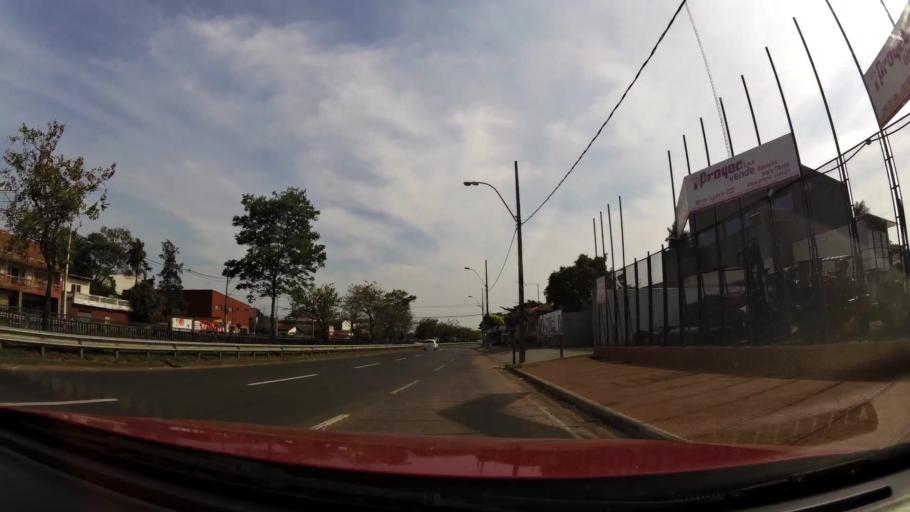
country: PY
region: Central
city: Fernando de la Mora
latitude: -25.3052
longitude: -57.5527
